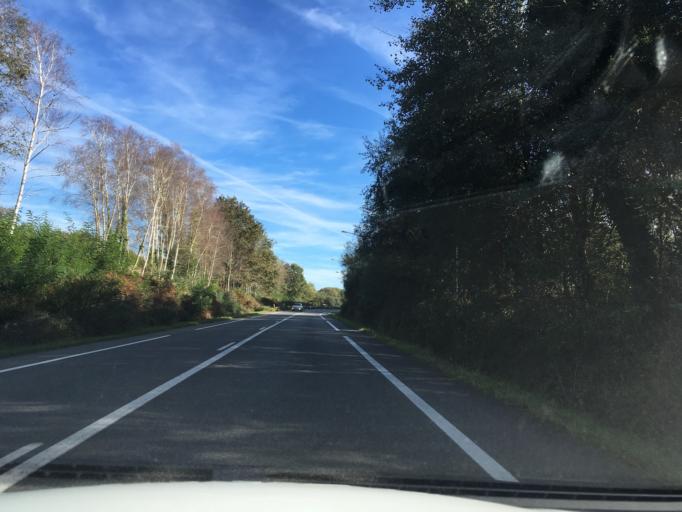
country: FR
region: Aquitaine
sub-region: Departement des Pyrenees-Atlantiques
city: Montardon
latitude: 43.3349
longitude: -0.3604
